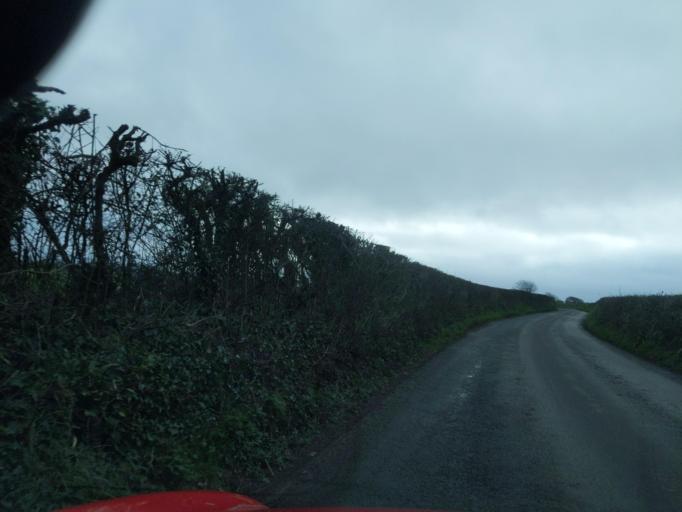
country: GB
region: England
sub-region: Devon
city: Wembury
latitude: 50.3319
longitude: -4.0935
